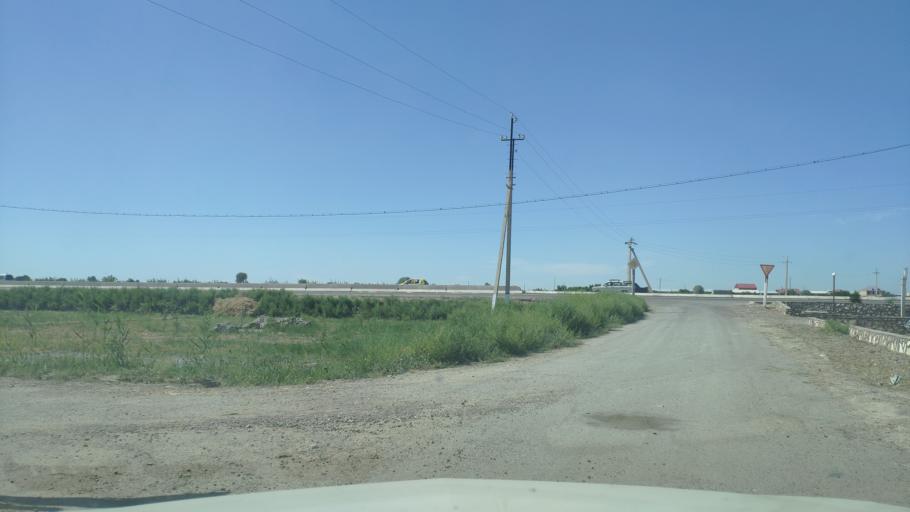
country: UZ
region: Bukhara
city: Bukhara
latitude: 39.7703
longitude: 64.3746
